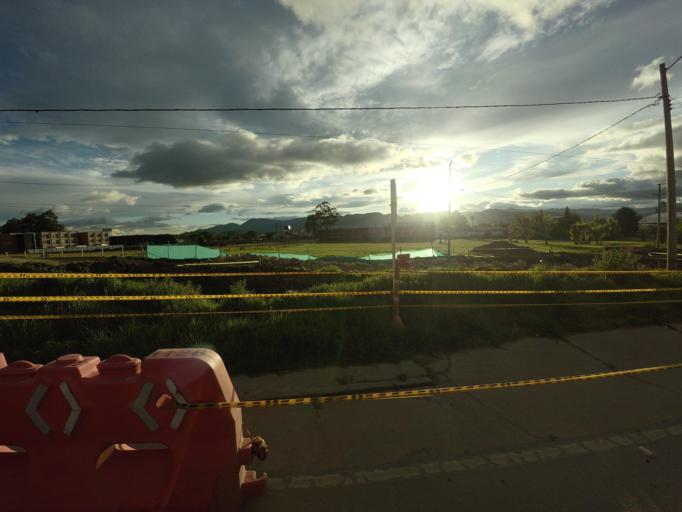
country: CO
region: Cundinamarca
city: Chia
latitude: 4.8362
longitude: -74.0289
